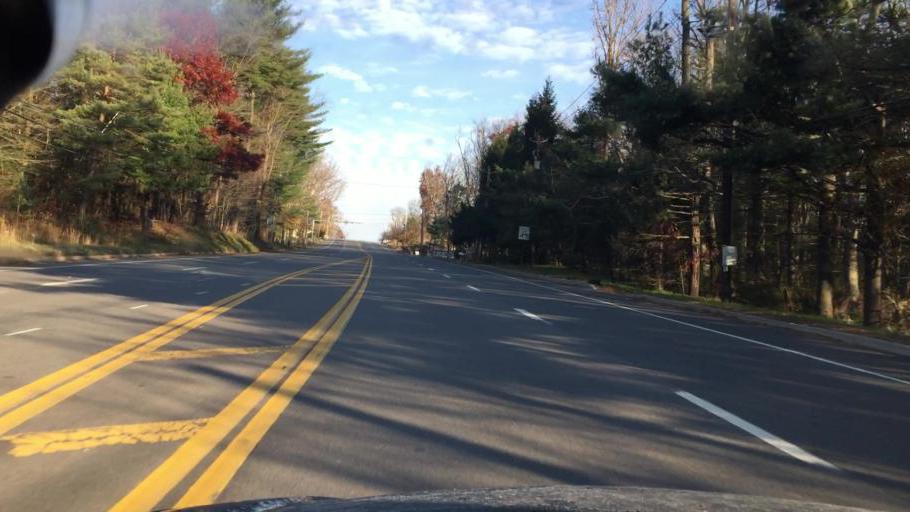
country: US
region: Pennsylvania
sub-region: Luzerne County
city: Oakdale
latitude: 41.0417
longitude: -75.9545
